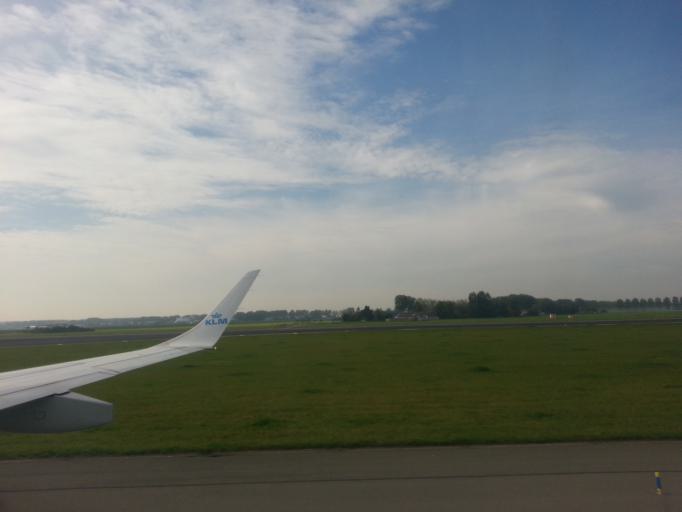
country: NL
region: North Holland
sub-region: Gemeente Haarlemmermeer
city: Hoofddorp
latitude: 52.3343
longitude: 4.7121
